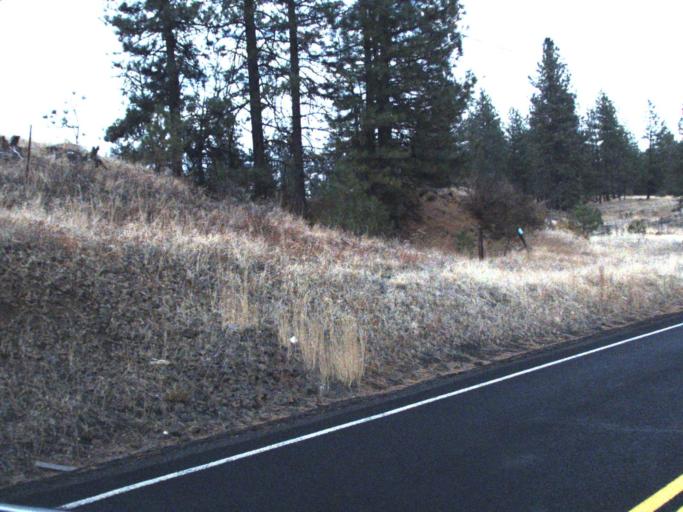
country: US
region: Washington
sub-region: Lincoln County
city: Davenport
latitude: 47.8236
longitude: -118.1898
